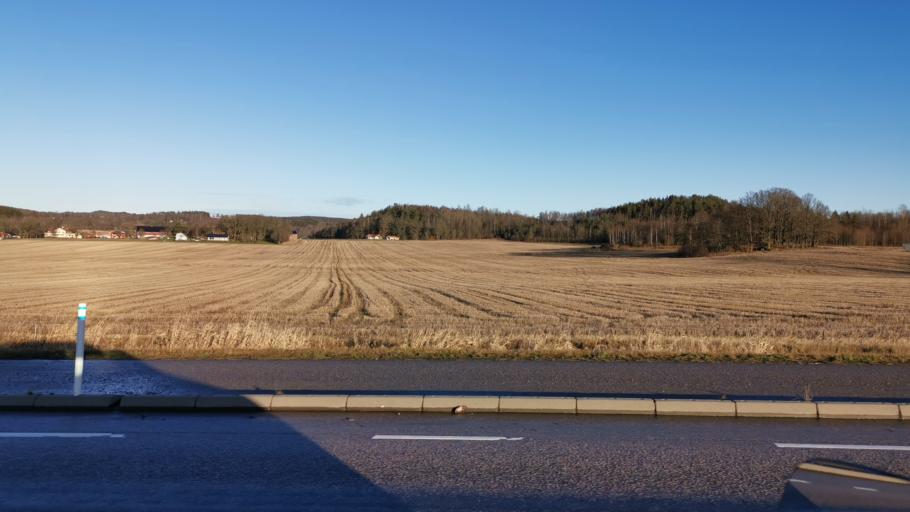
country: SE
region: Vaestra Goetaland
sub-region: Munkedals Kommun
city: Munkedal
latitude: 58.4811
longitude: 11.6400
